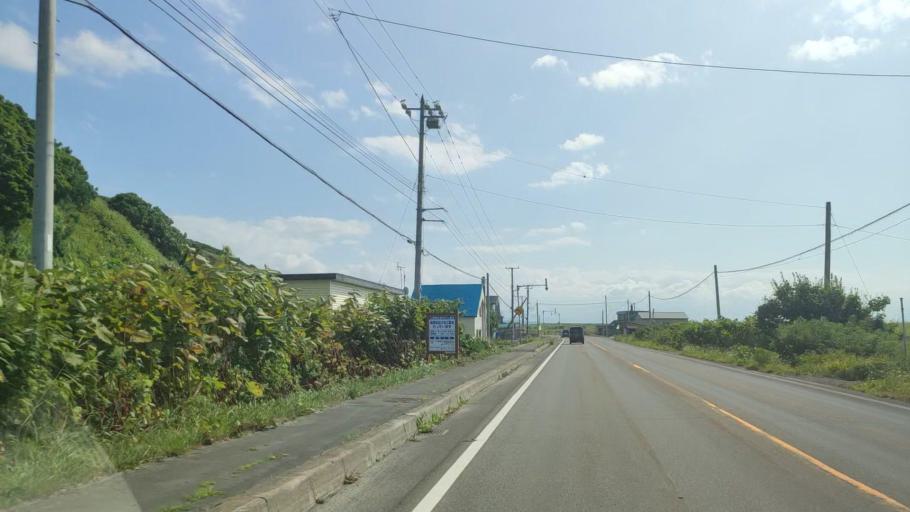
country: JP
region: Hokkaido
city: Rumoi
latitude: 43.9806
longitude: 141.6469
